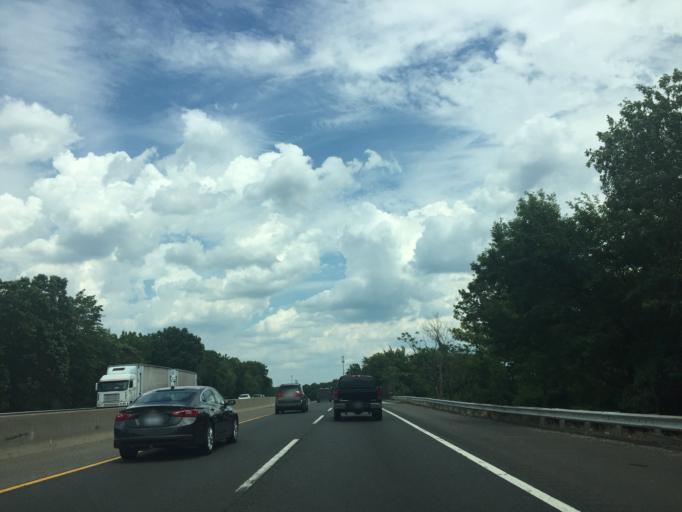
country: US
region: New Jersey
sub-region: Camden County
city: Lawnside
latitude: 39.8740
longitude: -75.0159
